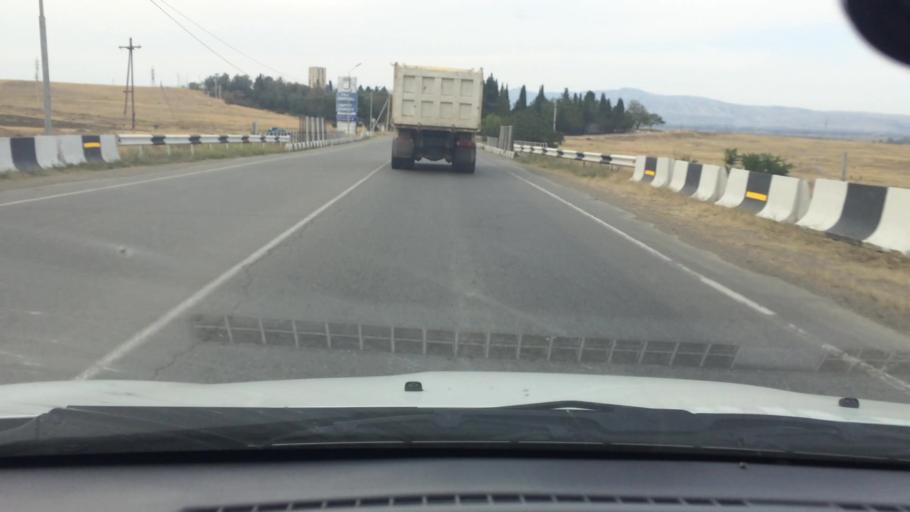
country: GE
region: Kvemo Kartli
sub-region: Marneuli
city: Marneuli
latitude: 41.5205
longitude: 44.7803
